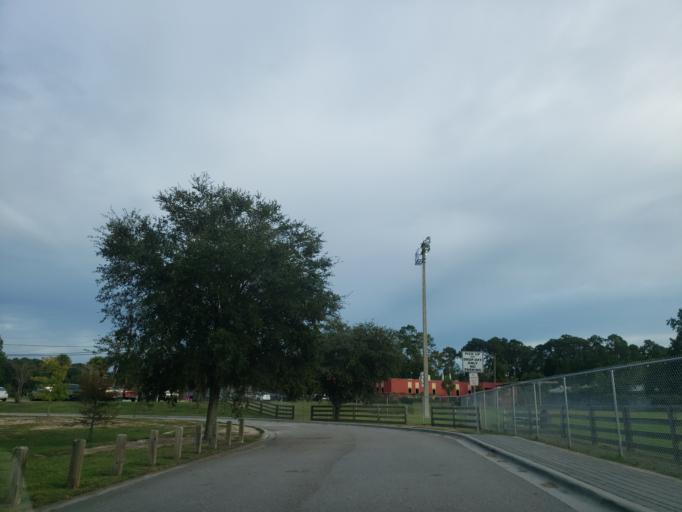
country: US
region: Georgia
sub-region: Chatham County
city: Isle of Hope
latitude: 32.0039
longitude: -81.0930
